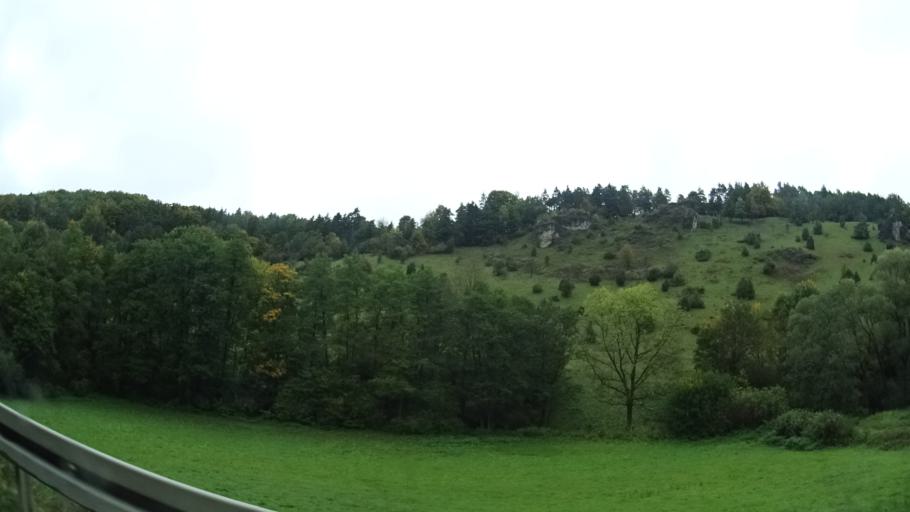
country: DE
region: Bavaria
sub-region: Upper Franconia
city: Wattendorf
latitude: 50.0268
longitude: 11.1026
